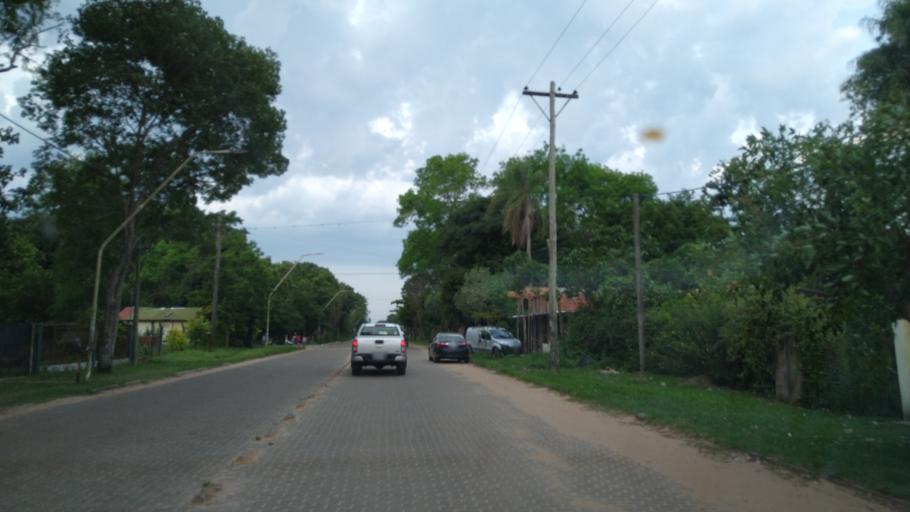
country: AR
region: Corrientes
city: Ituzaingo
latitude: -27.5911
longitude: -56.7003
